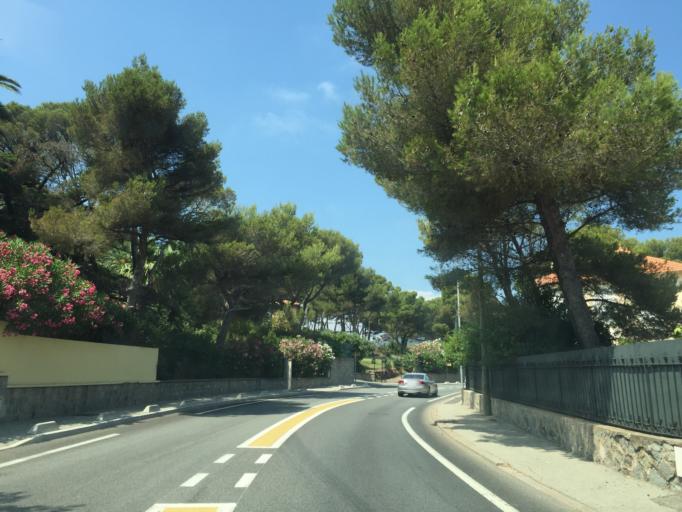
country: FR
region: Provence-Alpes-Cote d'Azur
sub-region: Departement du Var
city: Saint-Raphael
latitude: 43.4220
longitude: 6.8574
